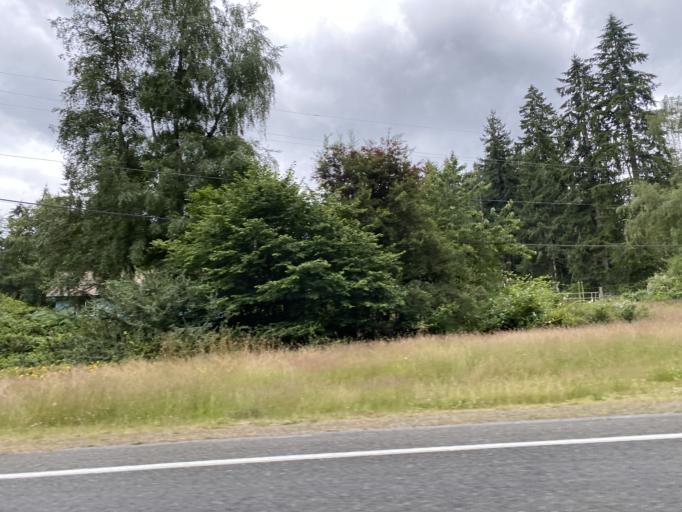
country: US
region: Washington
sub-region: Island County
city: Langley
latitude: 48.0402
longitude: -122.4256
